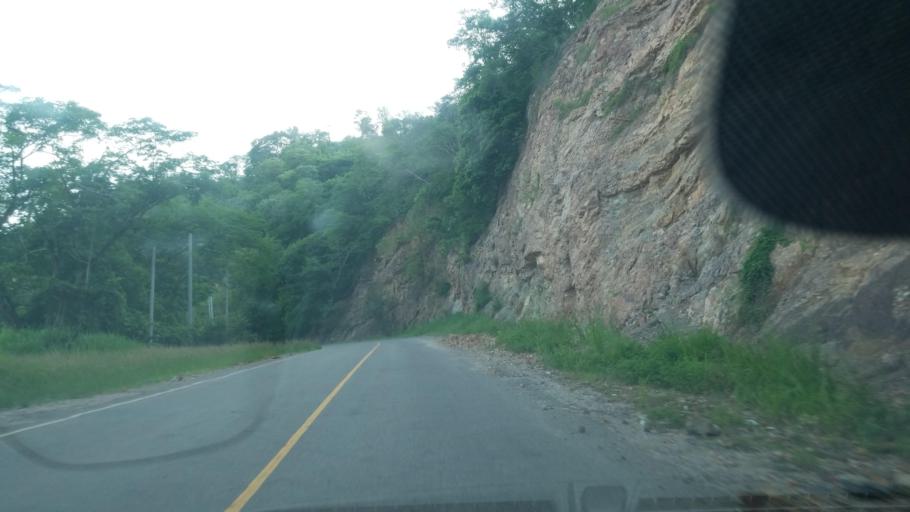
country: HN
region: Santa Barbara
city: Ilama
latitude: 15.0960
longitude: -88.2052
